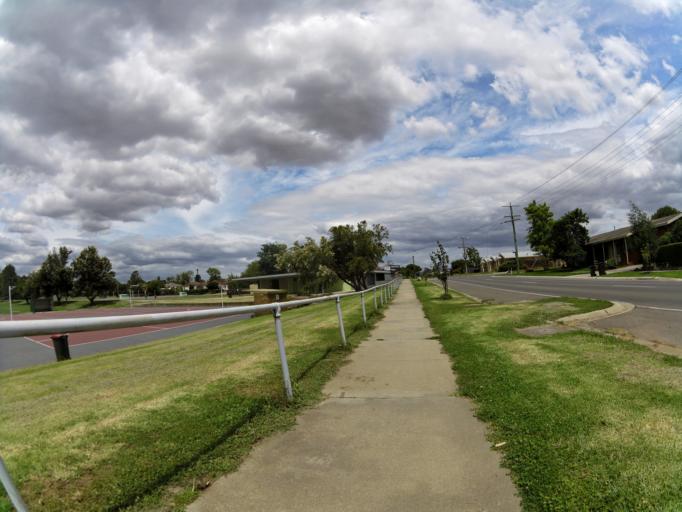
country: AU
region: Victoria
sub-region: Latrobe
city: Traralgon
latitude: -38.1883
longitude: 146.5344
